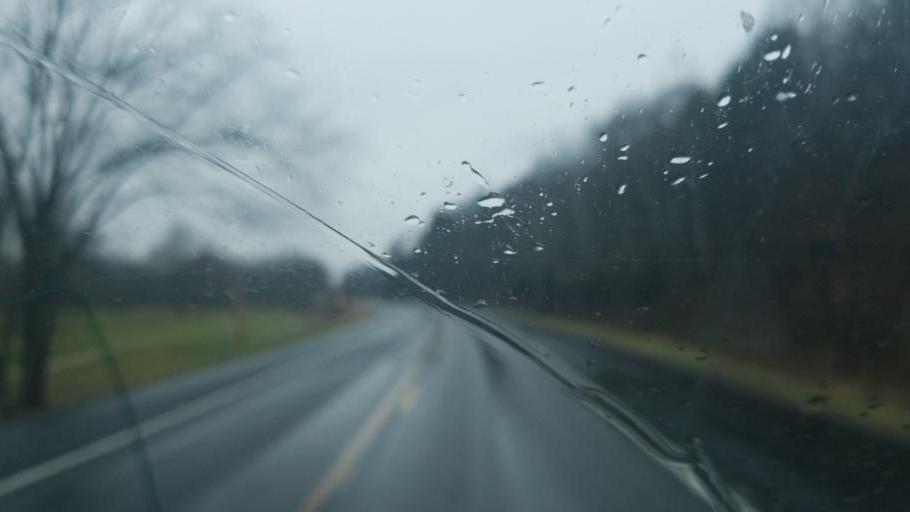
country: US
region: Indiana
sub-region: Brown County
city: Nashville
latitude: 39.1960
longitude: -86.2056
